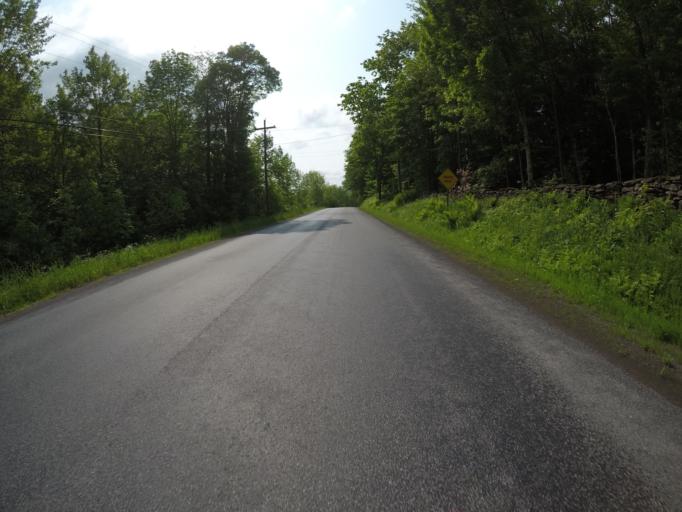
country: US
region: New York
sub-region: Delaware County
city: Stamford
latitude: 42.1587
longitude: -74.6580
